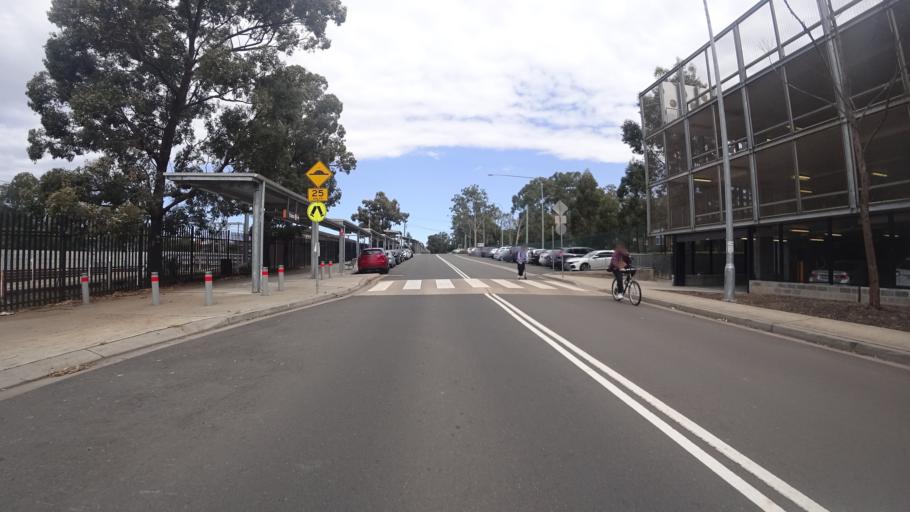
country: AU
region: New South Wales
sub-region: Campbelltown Municipality
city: Glenfield
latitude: -33.9696
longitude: 150.8956
